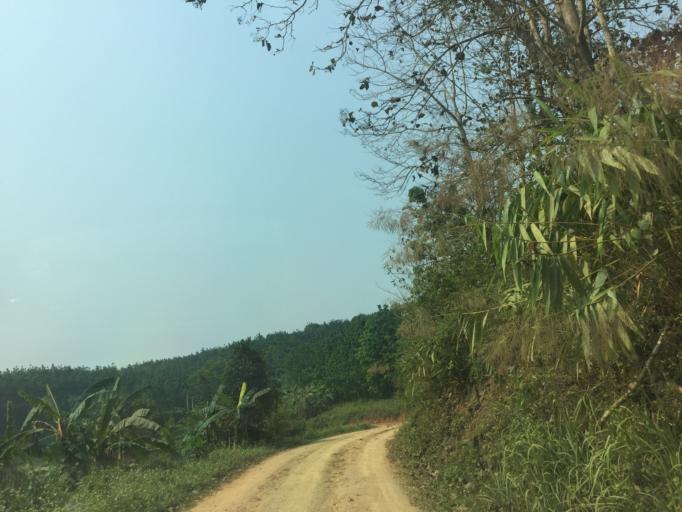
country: TH
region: Phayao
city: Phu Sang
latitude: 19.6026
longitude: 100.5339
